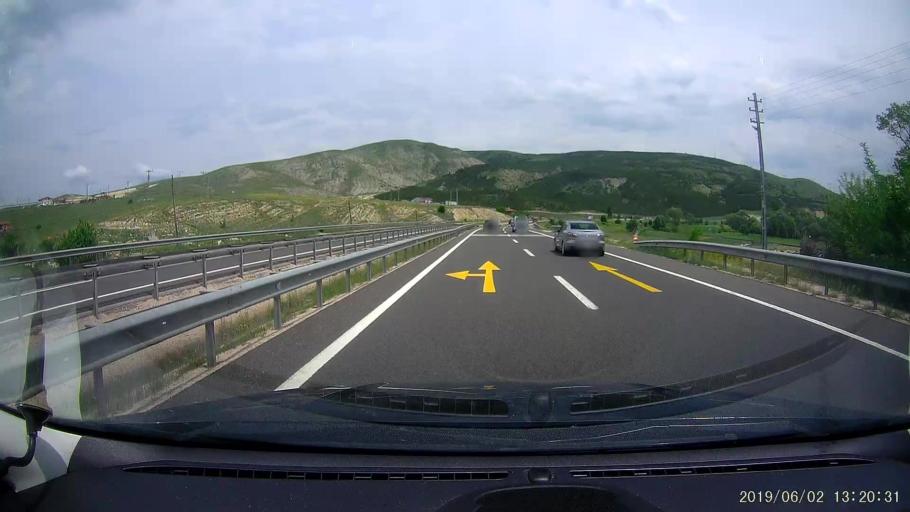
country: TR
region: Cankiri
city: Cerkes
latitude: 40.8418
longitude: 32.7617
